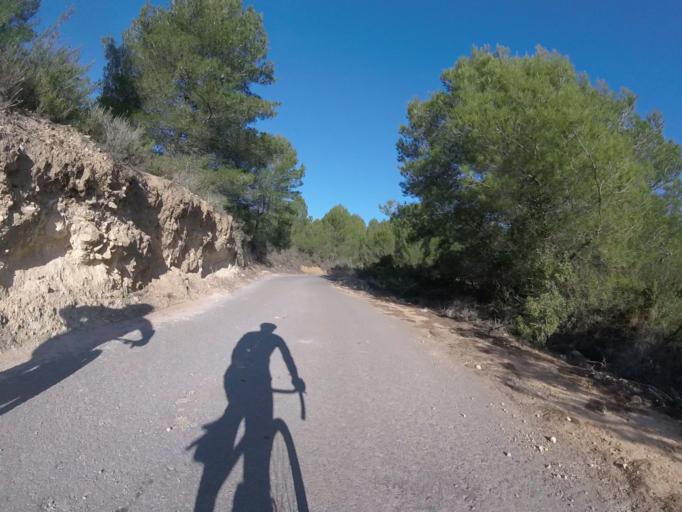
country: ES
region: Valencia
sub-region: Provincia de Castello
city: Alcala de Xivert
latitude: 40.2725
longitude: 0.2064
